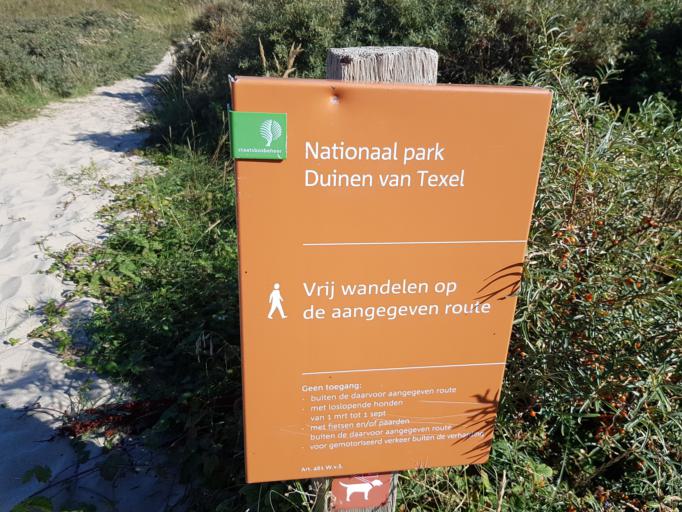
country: NL
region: North Holland
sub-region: Gemeente Texel
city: Den Burg
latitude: 53.0670
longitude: 4.7275
